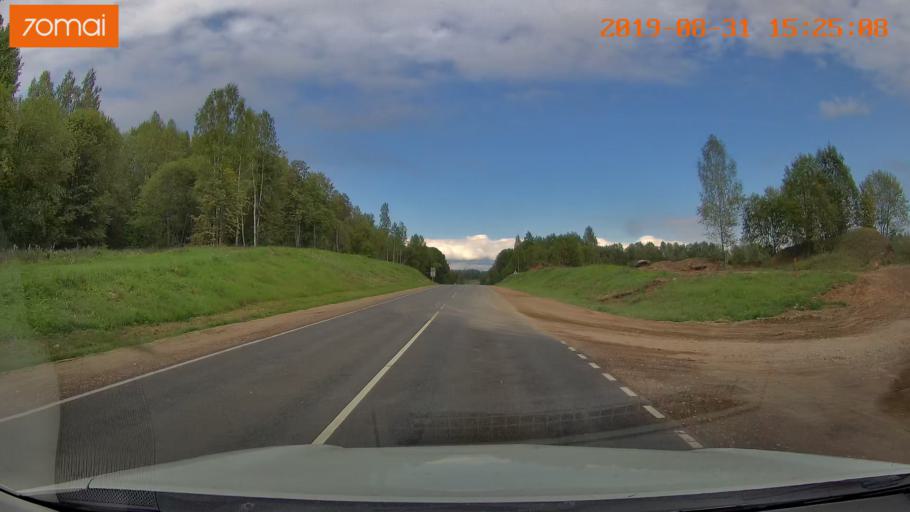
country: RU
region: Kaluga
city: Baryatino
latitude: 54.5373
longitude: 34.5152
